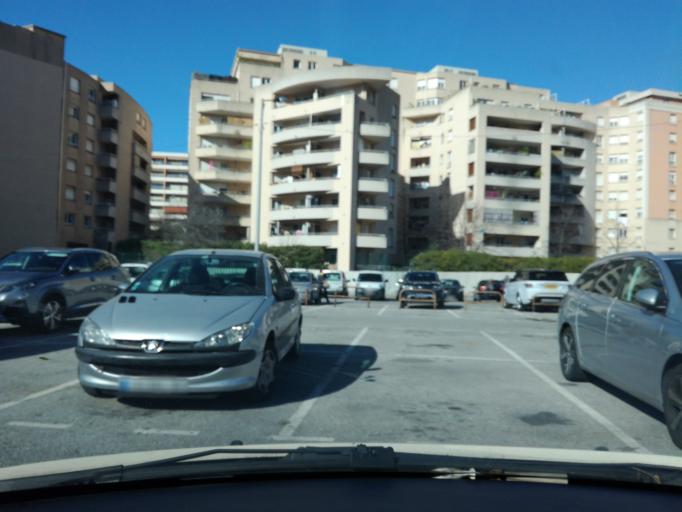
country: FR
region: Provence-Alpes-Cote d'Azur
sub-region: Departement des Alpes-Maritimes
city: Saint-Andre-de-la-Roche
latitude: 43.7125
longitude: 7.2860
